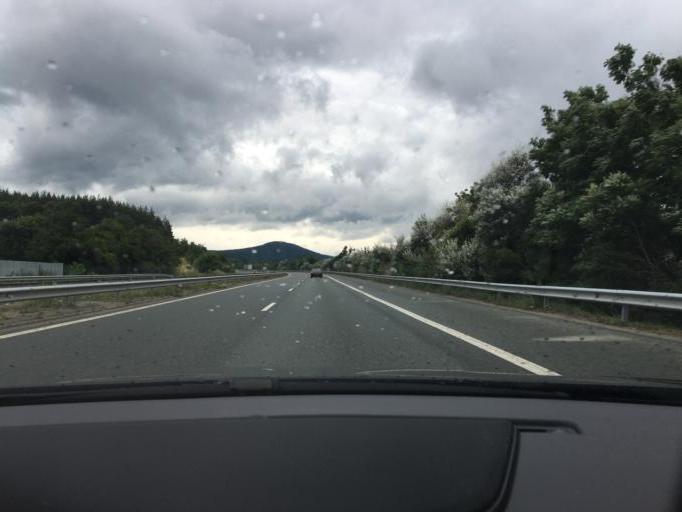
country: BG
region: Pernik
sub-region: Obshtina Pernik
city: Pernik
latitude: 42.5578
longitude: 23.1179
